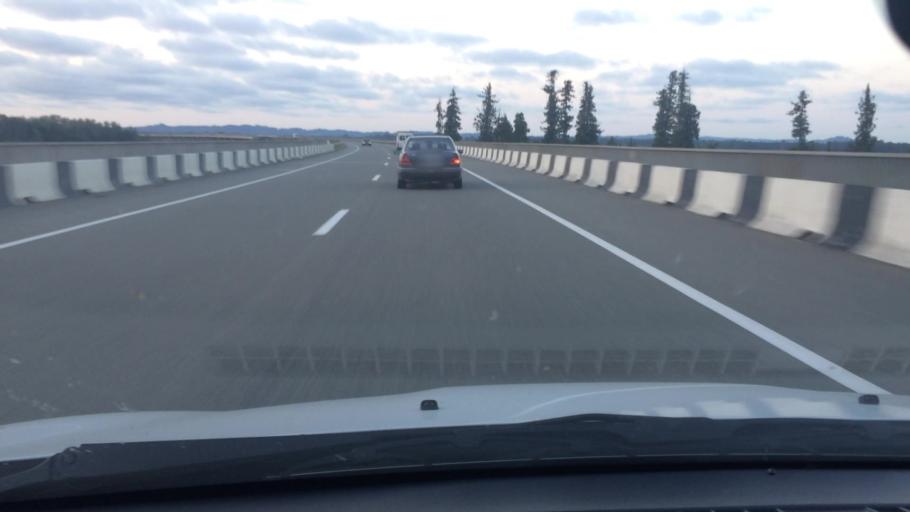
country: GE
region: Ajaria
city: Ochkhamuri
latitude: 41.8600
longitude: 41.8379
